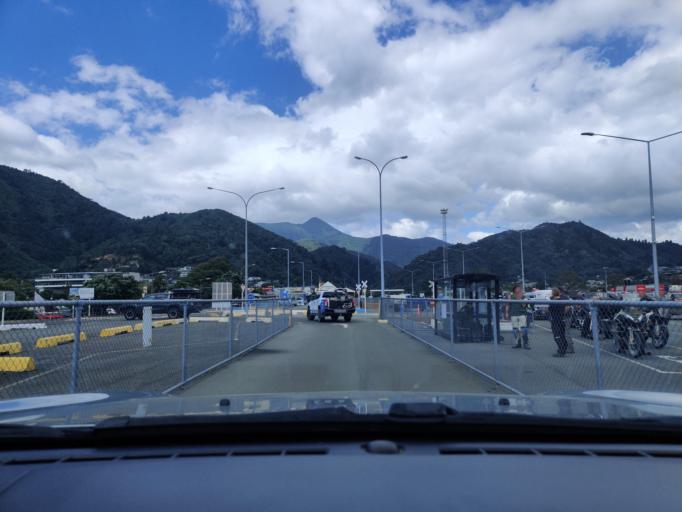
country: NZ
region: Marlborough
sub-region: Marlborough District
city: Picton
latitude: -41.2867
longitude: 174.0046
